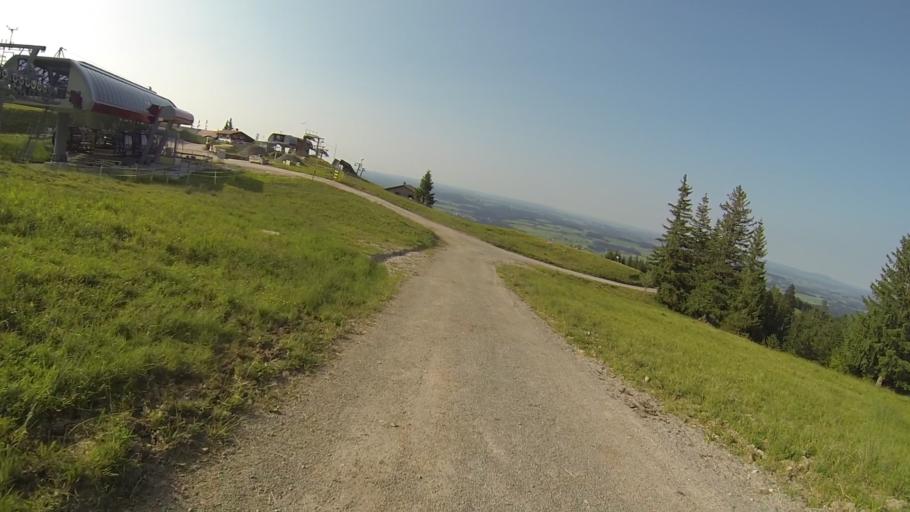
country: DE
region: Bavaria
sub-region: Swabia
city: Nesselwang
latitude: 47.6055
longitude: 10.4980
